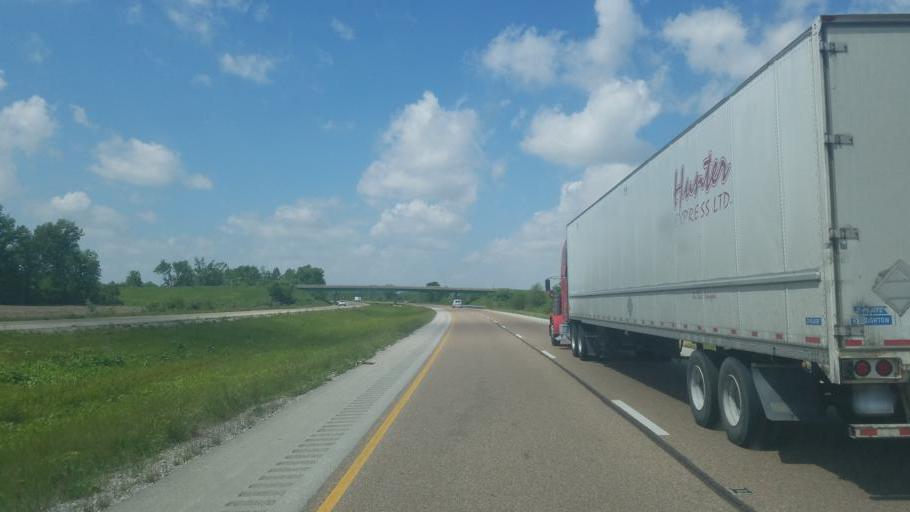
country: US
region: Illinois
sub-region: Cumberland County
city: Greenup
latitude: 39.2740
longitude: -88.1070
